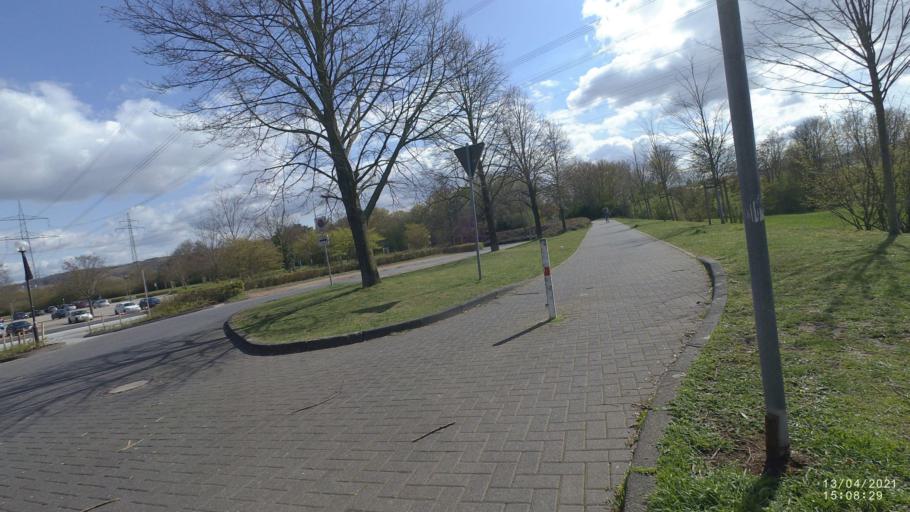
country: DE
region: Rheinland-Pfalz
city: Mulheim-Karlich
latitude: 50.3946
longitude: 7.4973
